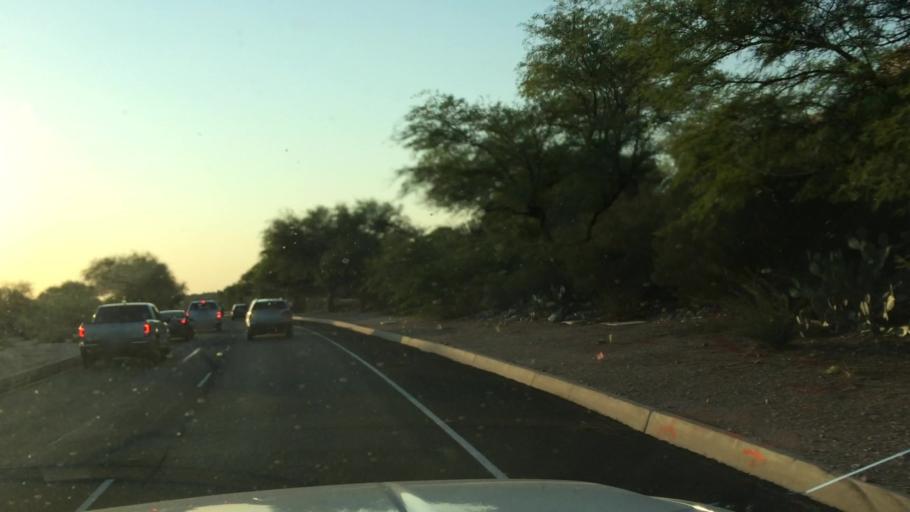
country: US
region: Arizona
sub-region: Pima County
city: Catalina Foothills
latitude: 32.3181
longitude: -110.9149
